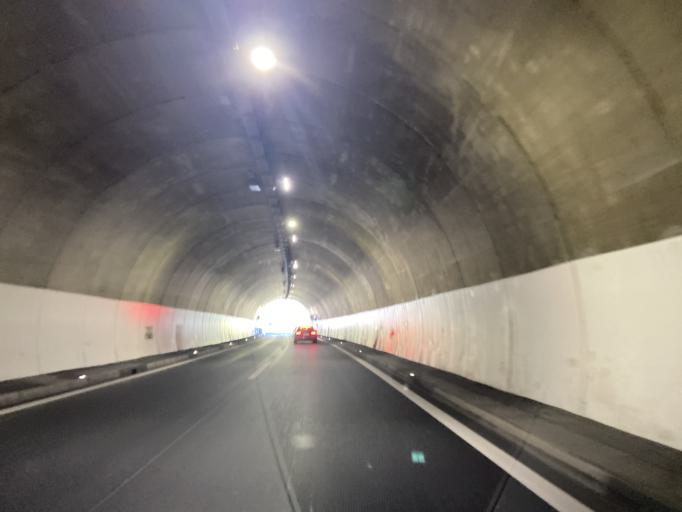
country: CH
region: Schwyz
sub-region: Bezirk Schwyz
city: Arth
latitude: 47.0529
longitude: 8.5250
